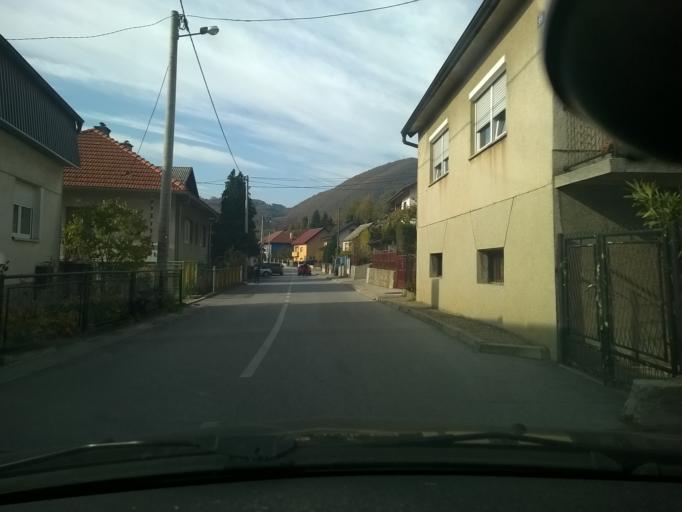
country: HR
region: Krapinsko-Zagorska
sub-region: Grad Krapina
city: Krapina
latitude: 46.1810
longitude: 15.8638
